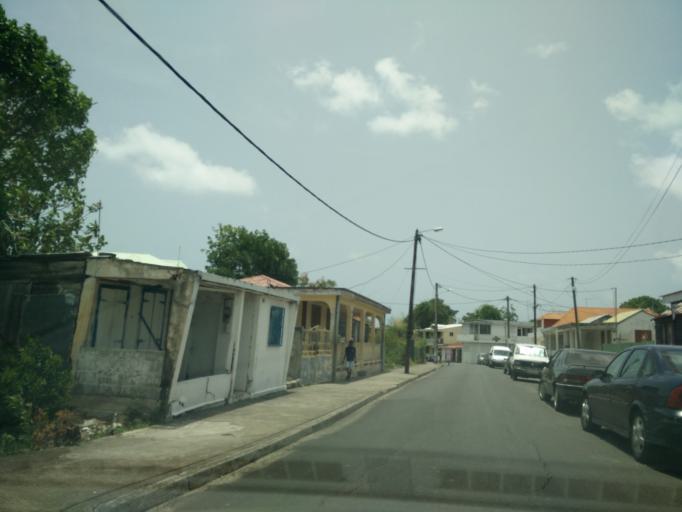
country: GP
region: Guadeloupe
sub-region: Guadeloupe
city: Anse-Bertrand
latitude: 16.4720
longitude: -61.5082
